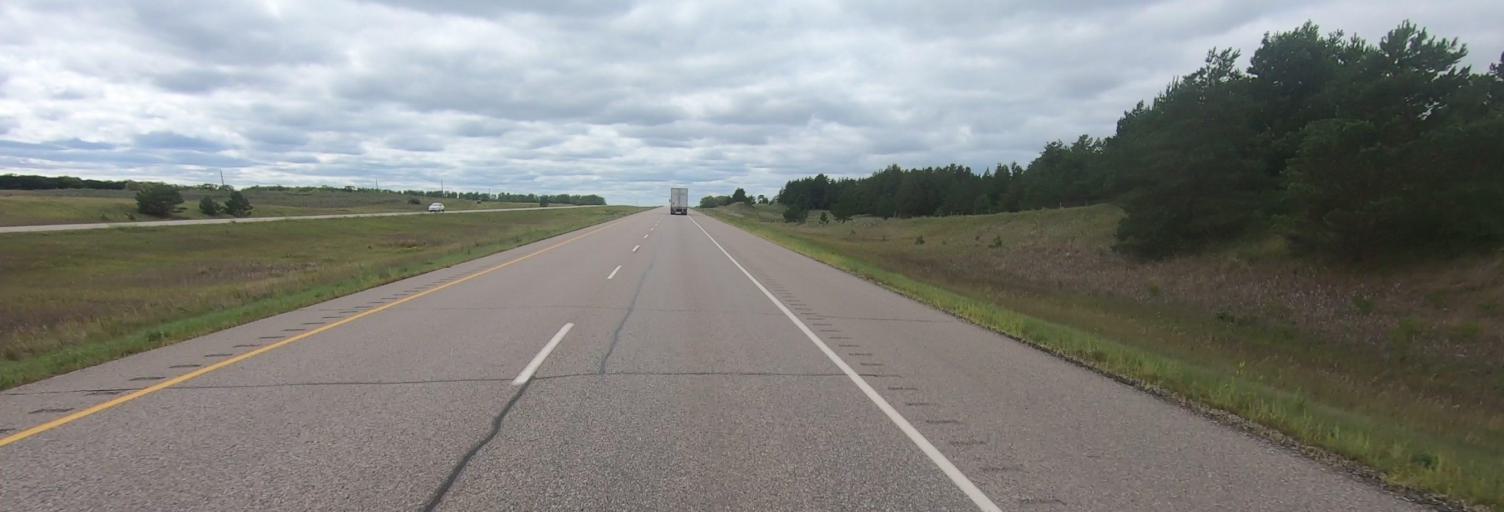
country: CA
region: Manitoba
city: Carberry
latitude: 49.9015
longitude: -99.2721
